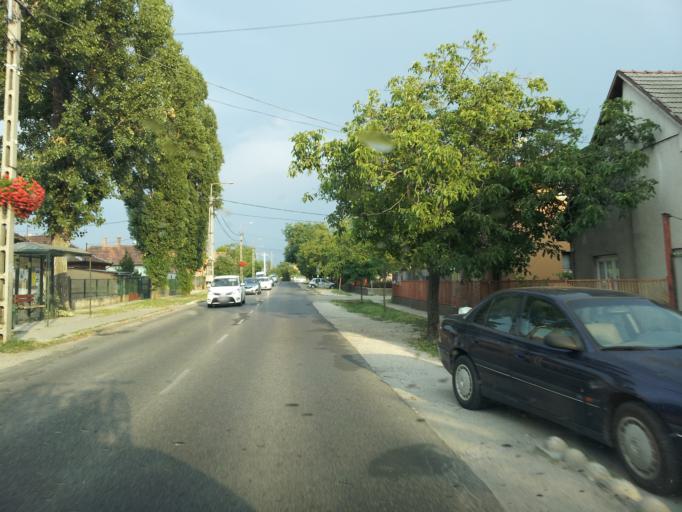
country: HU
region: Pest
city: Dunaharaszti
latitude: 47.3493
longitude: 19.1070
